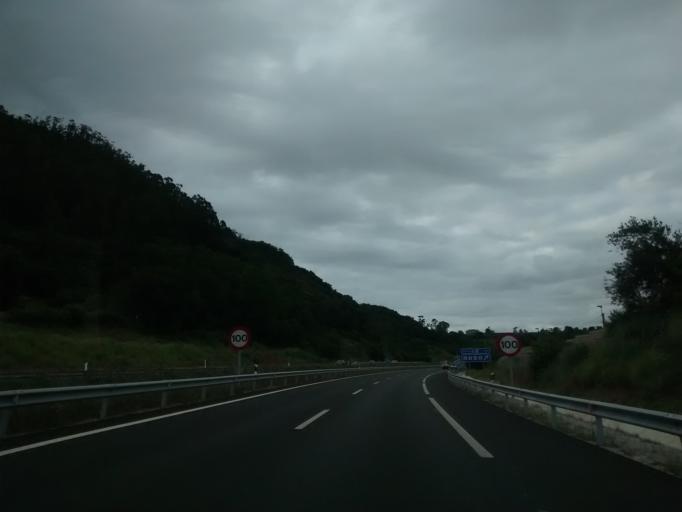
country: ES
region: Cantabria
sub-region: Provincia de Cantabria
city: Lierganes
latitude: 43.3800
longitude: -3.7482
